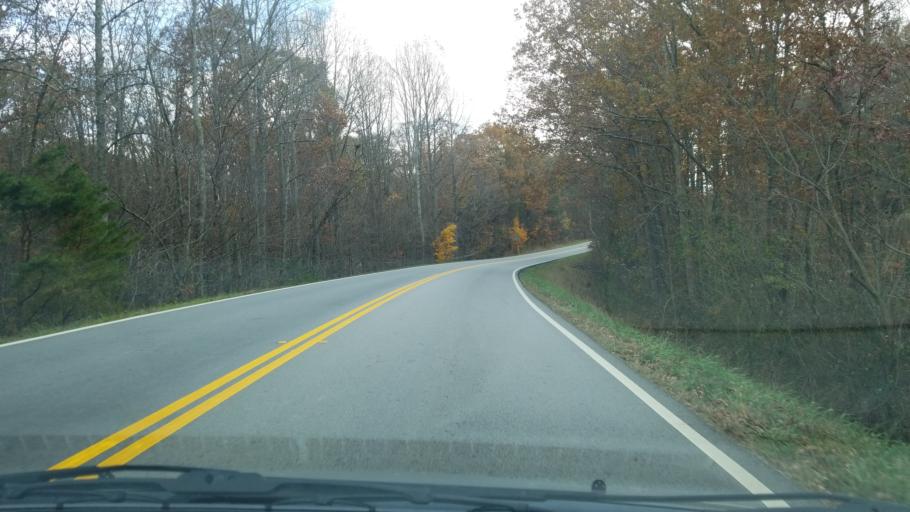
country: US
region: Georgia
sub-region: Dade County
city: Trenton
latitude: 34.8244
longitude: -85.5015
